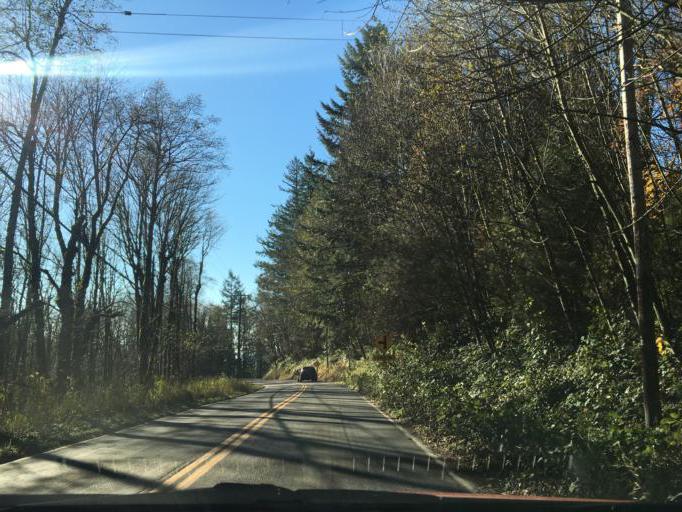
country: US
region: Oregon
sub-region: Washington County
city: Oak Hills
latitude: 45.5823
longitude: -122.8005
